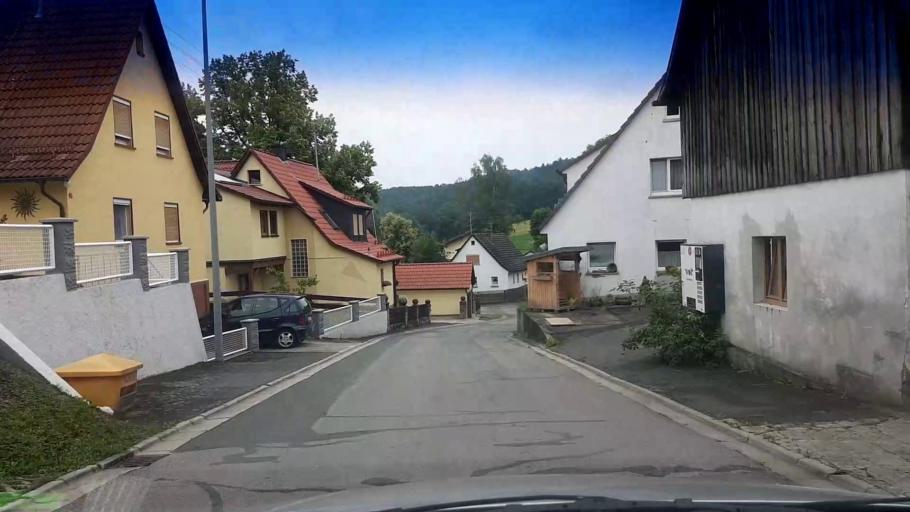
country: DE
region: Bavaria
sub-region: Upper Franconia
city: Mainleus
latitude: 50.0814
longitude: 11.3406
